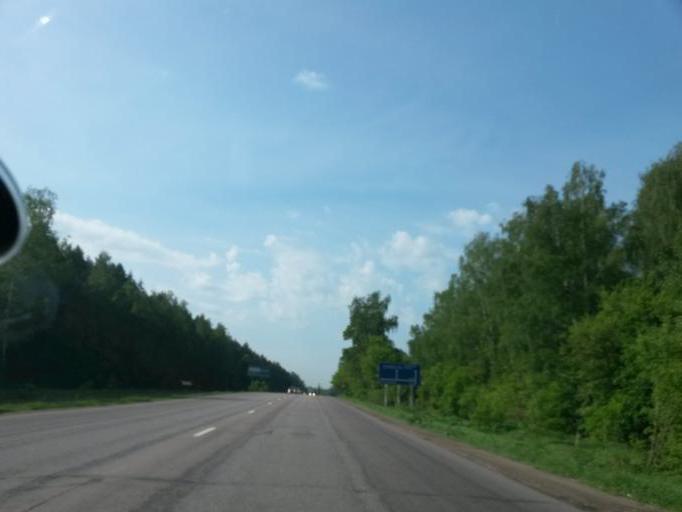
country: RU
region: Moskovskaya
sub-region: Chekhovskiy Rayon
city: Chekhov
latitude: 55.1955
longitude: 37.5045
